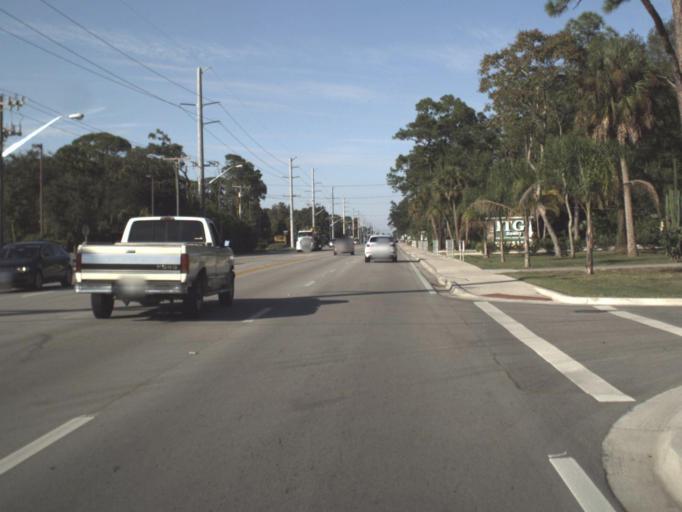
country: US
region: Florida
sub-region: Brevard County
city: June Park
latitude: 28.0828
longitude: -80.6725
